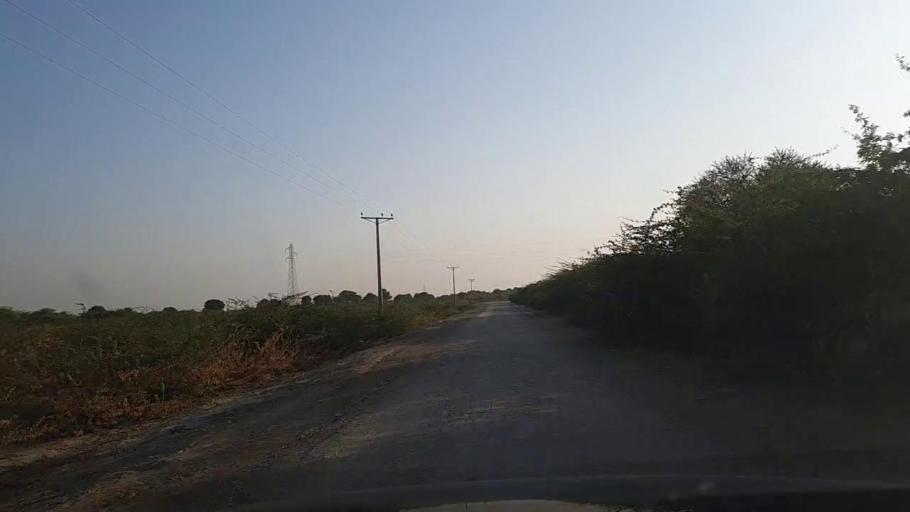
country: PK
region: Sindh
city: Naukot
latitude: 24.8905
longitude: 69.3342
